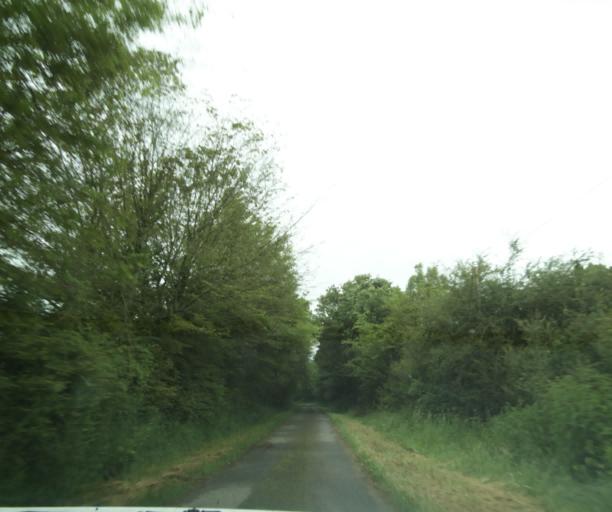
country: FR
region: Bourgogne
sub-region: Departement de Saone-et-Loire
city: Palinges
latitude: 46.5730
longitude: 4.2069
